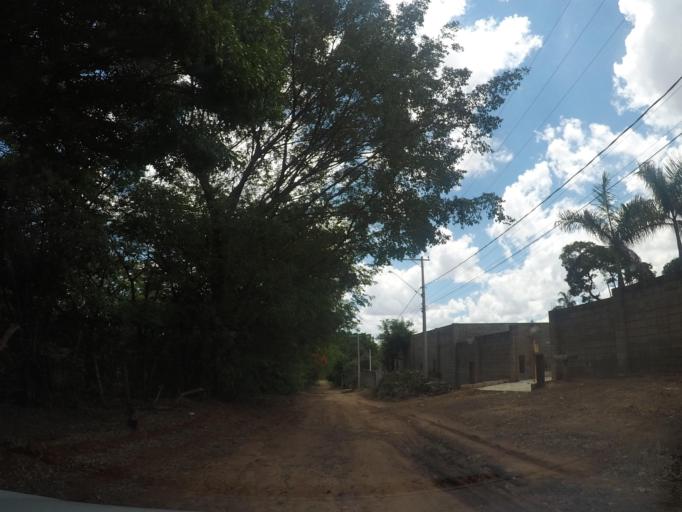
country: BR
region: Sao Paulo
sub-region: Hortolandia
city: Hortolandia
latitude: -22.8425
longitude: -47.2293
